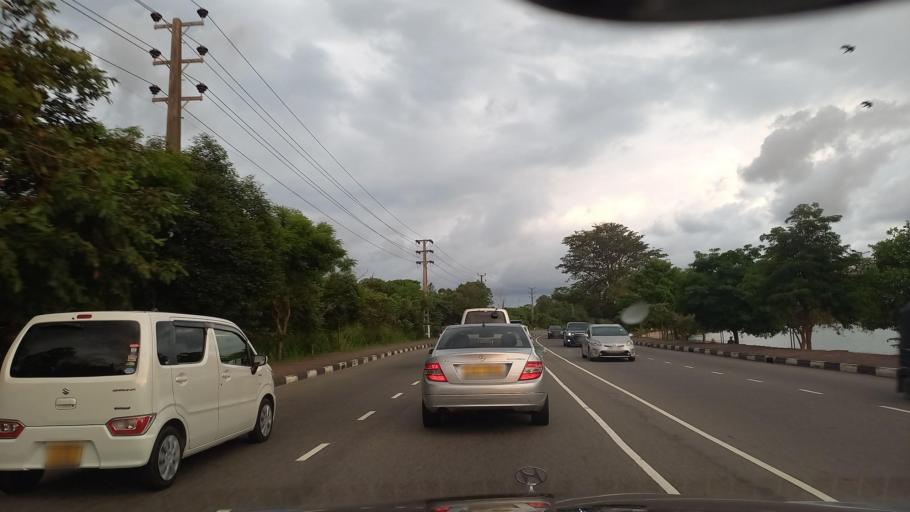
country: LK
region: Western
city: Battaramulla South
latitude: 6.8833
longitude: 79.9265
